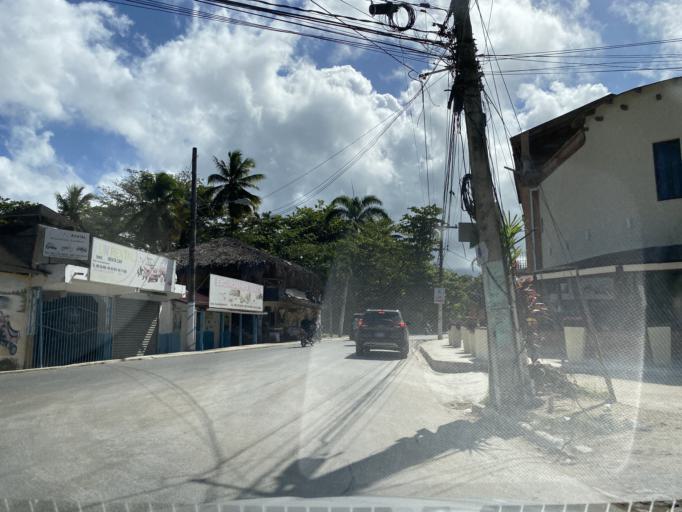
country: DO
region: Samana
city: Las Terrenas
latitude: 19.3210
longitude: -69.5406
